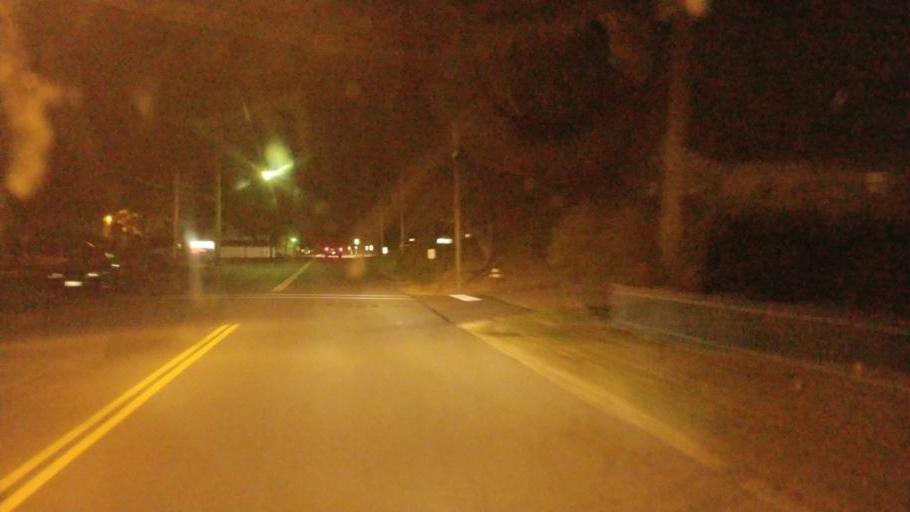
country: US
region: Ohio
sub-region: Ashland County
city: Ashland
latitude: 40.8068
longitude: -82.1966
